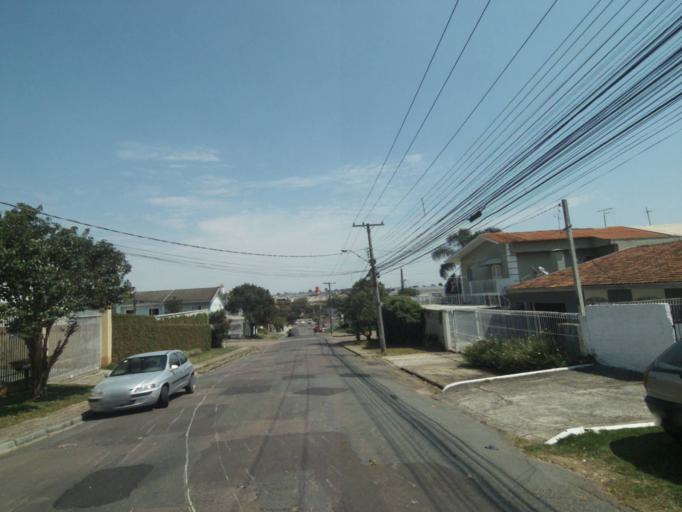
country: BR
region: Parana
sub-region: Curitiba
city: Curitiba
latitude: -25.4778
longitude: -49.3154
